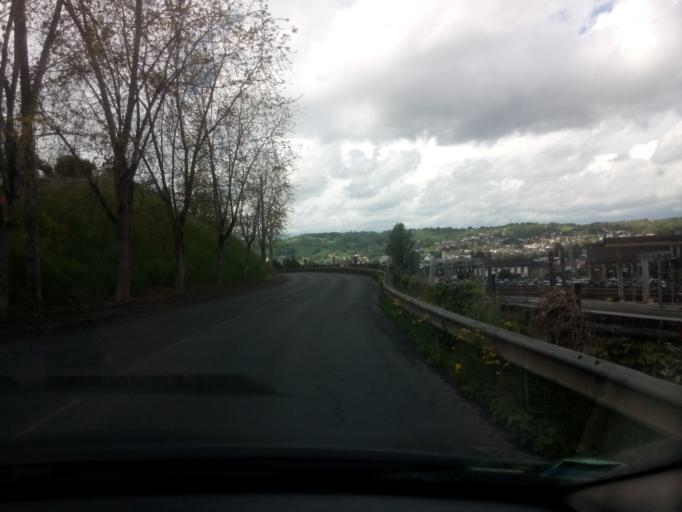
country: FR
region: Limousin
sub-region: Departement de la Correze
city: Brive-la-Gaillarde
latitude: 45.1522
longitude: 1.5256
